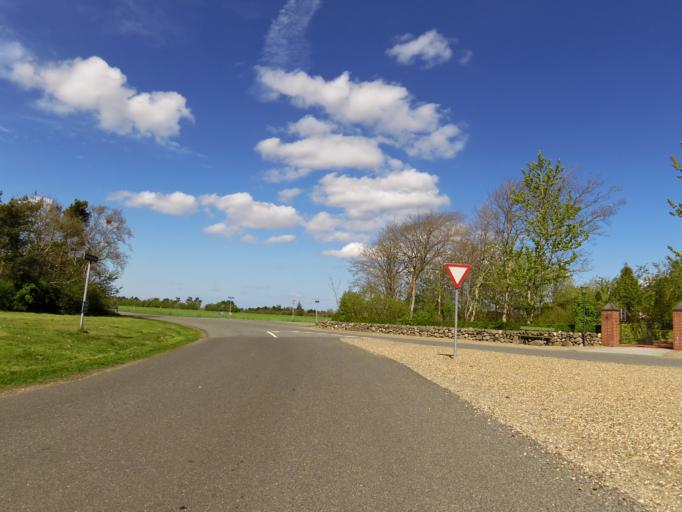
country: DK
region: Central Jutland
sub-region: Skive Kommune
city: Skive
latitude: 56.4612
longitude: 8.9751
